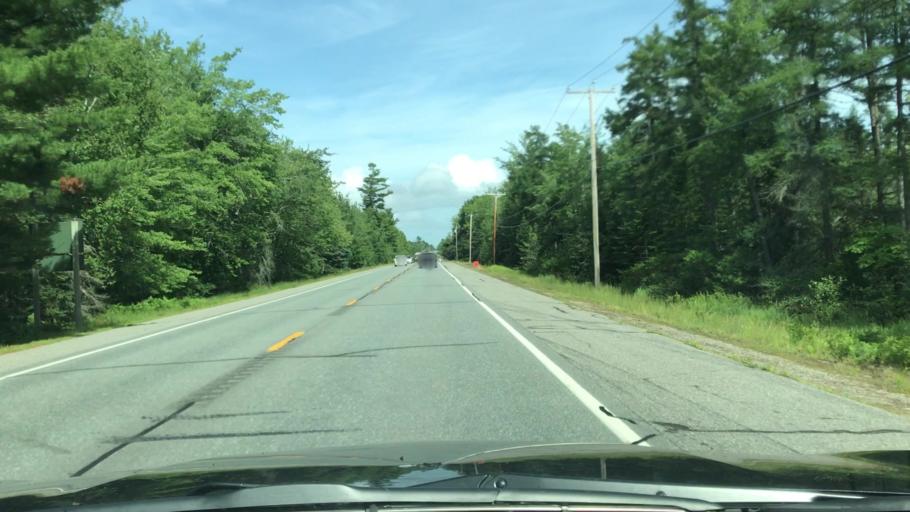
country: US
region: Maine
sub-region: Hancock County
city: Ellsworth
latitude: 44.5395
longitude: -68.4674
